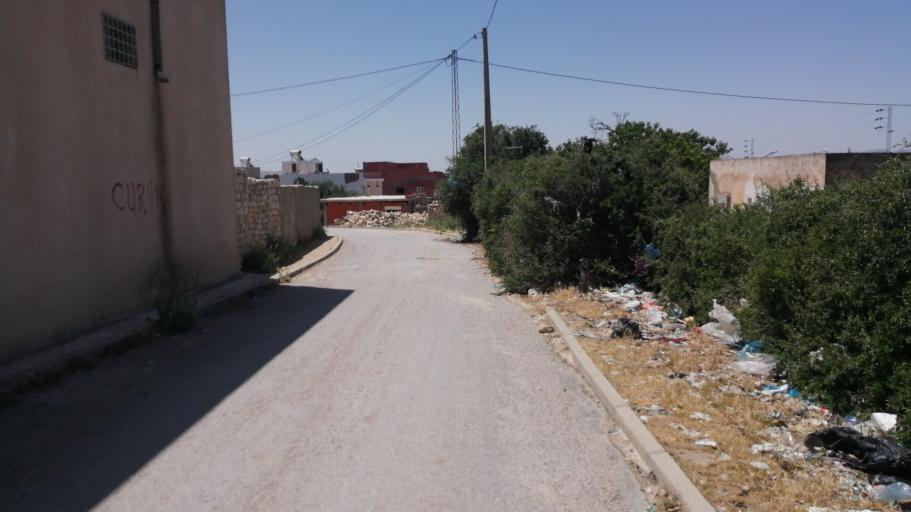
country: TN
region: Silyanah
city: Maktar
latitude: 35.8509
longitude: 9.2039
